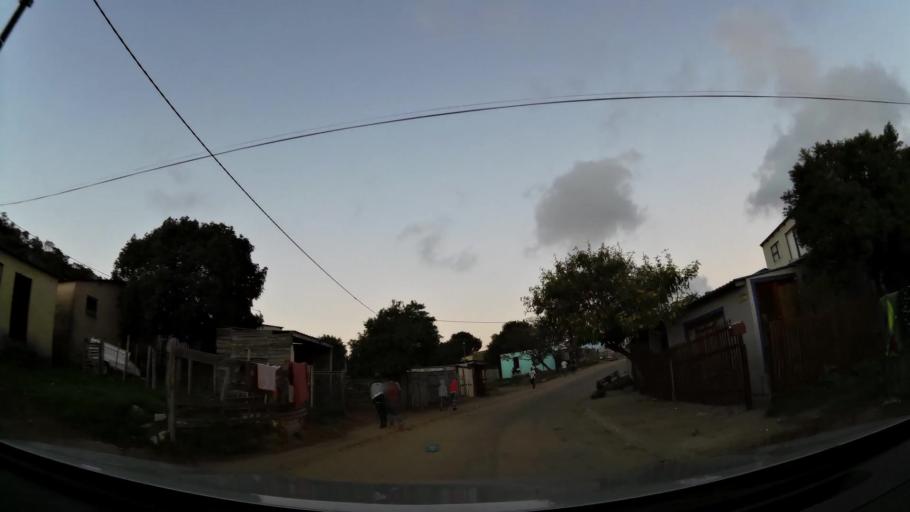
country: ZA
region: Western Cape
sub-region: Eden District Municipality
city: Knysna
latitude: -34.0260
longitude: 22.8194
